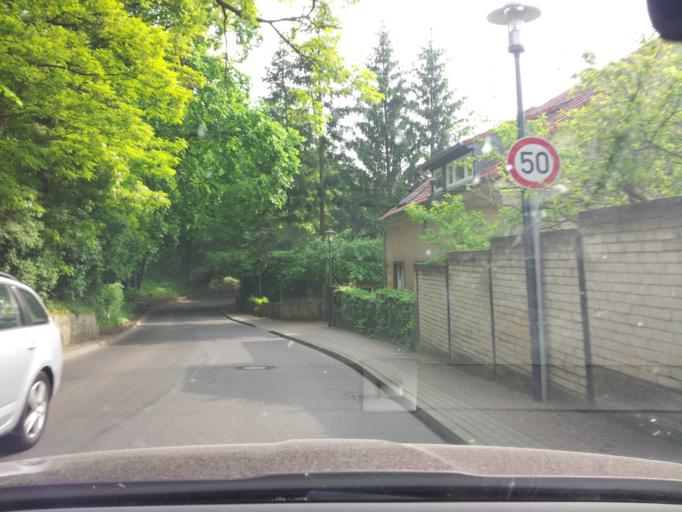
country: DE
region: Brandenburg
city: Fichtenwalde
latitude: 52.3115
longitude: 12.9293
